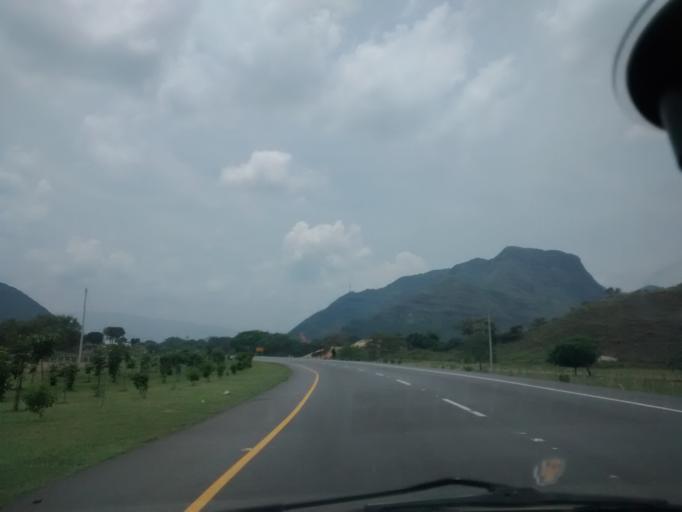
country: CO
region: Tolima
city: Valle de San Juan
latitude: 4.2774
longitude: -75.0071
